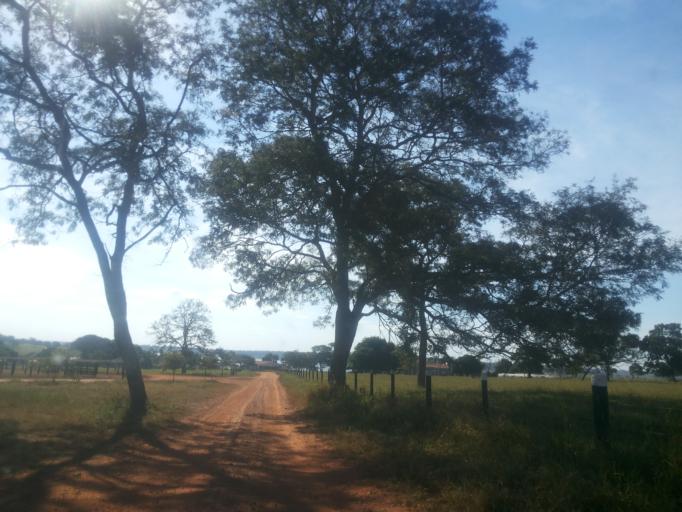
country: BR
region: Minas Gerais
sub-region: Santa Vitoria
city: Santa Vitoria
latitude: -19.0104
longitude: -50.4112
